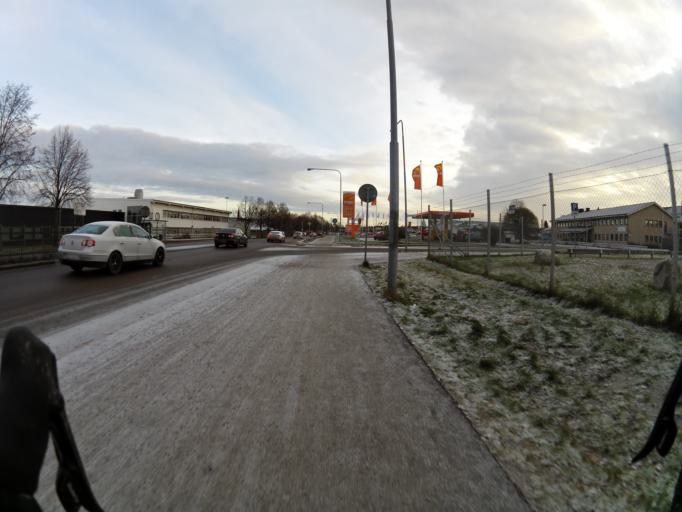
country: SE
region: Gaevleborg
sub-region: Gavle Kommun
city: Gavle
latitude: 60.6611
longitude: 17.1590
